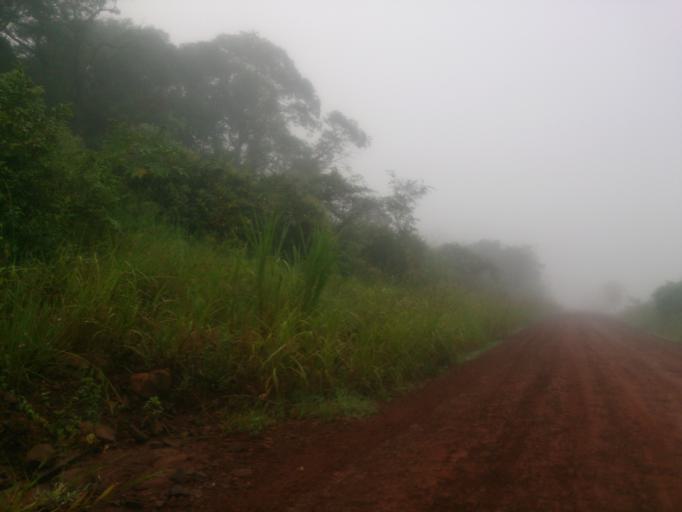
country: AR
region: Misiones
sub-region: Departamento de Obera
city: Obera
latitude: -27.4704
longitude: -55.1063
